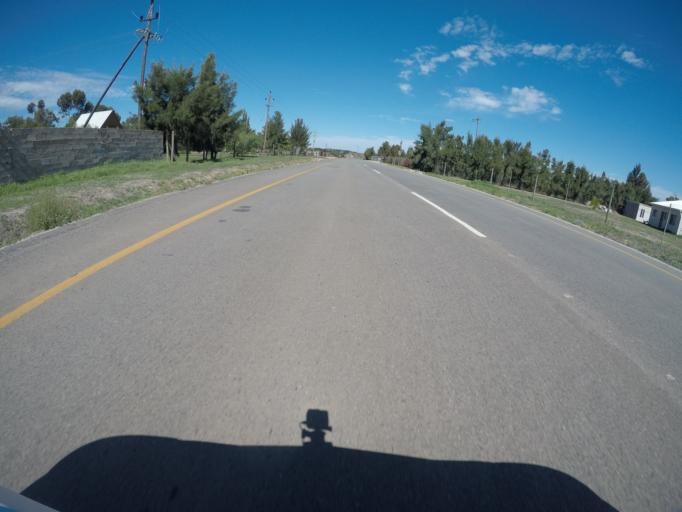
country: ZA
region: Western Cape
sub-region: West Coast District Municipality
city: Malmesbury
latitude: -33.5782
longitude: 18.6469
